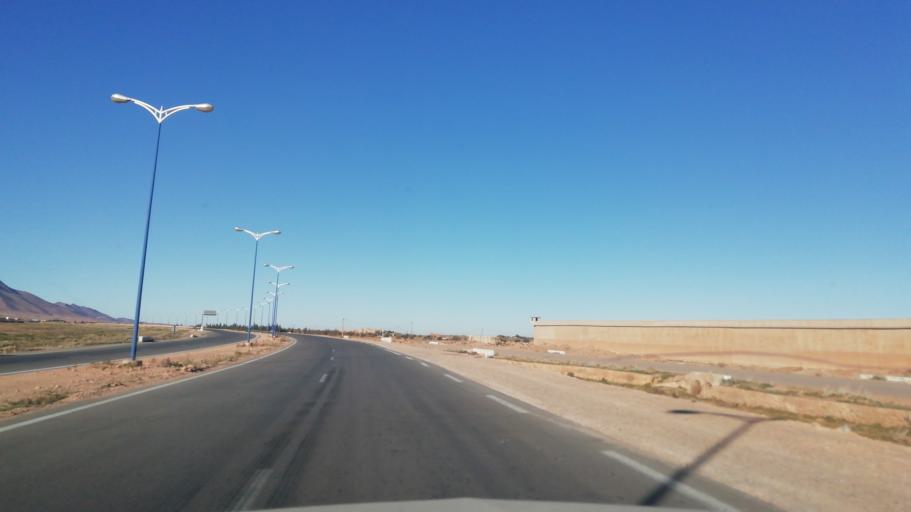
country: DZ
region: Wilaya de Naama
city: Naama
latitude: 33.5580
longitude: -0.2369
